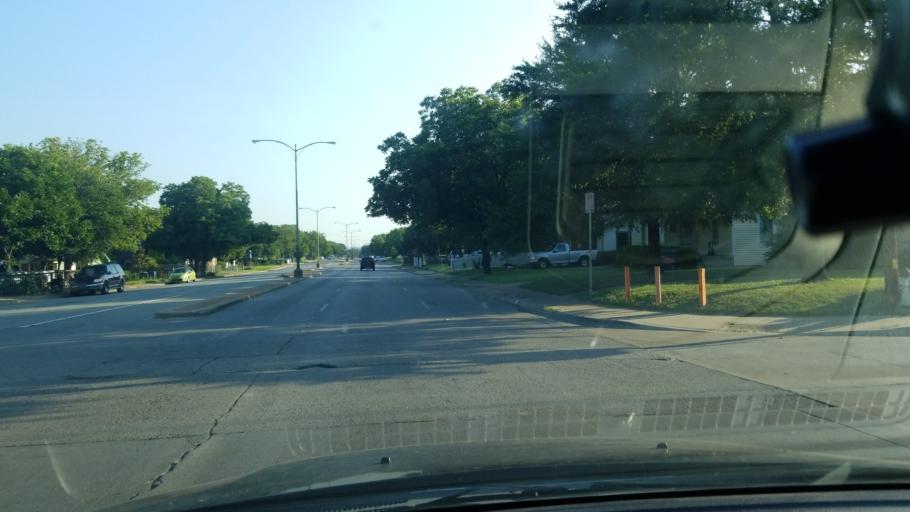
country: US
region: Texas
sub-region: Dallas County
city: Dallas
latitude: 32.7250
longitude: -96.8144
